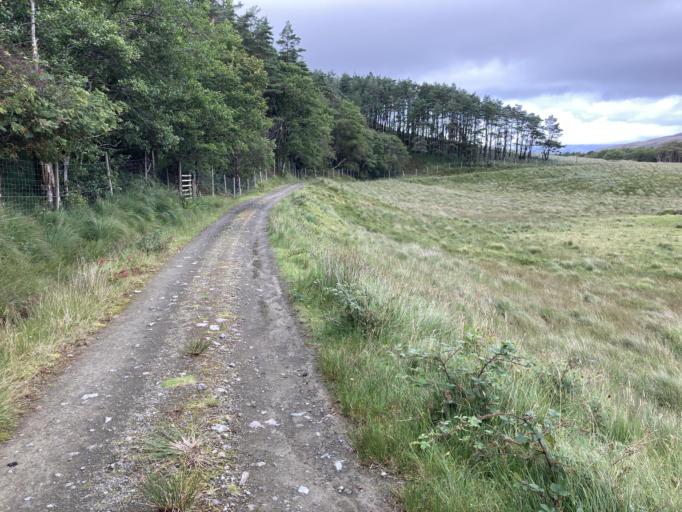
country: GB
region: Scotland
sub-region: Highland
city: Isle of Skye
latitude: 57.0153
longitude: -6.3202
